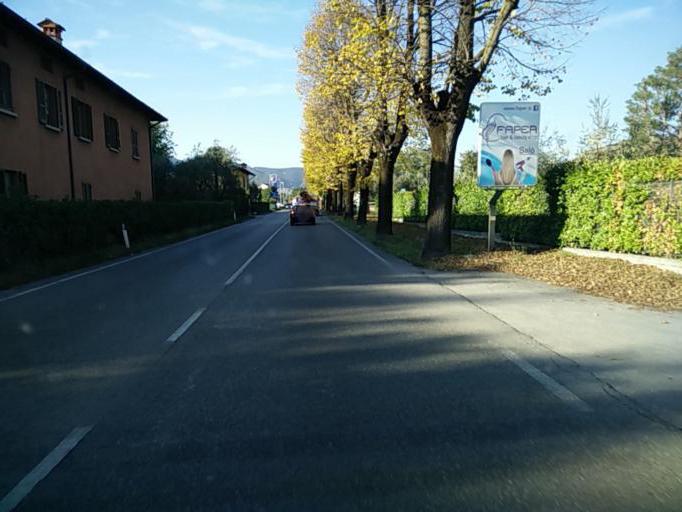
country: IT
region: Lombardy
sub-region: Provincia di Brescia
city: Cunettone-Villa
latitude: 45.5845
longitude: 10.5192
